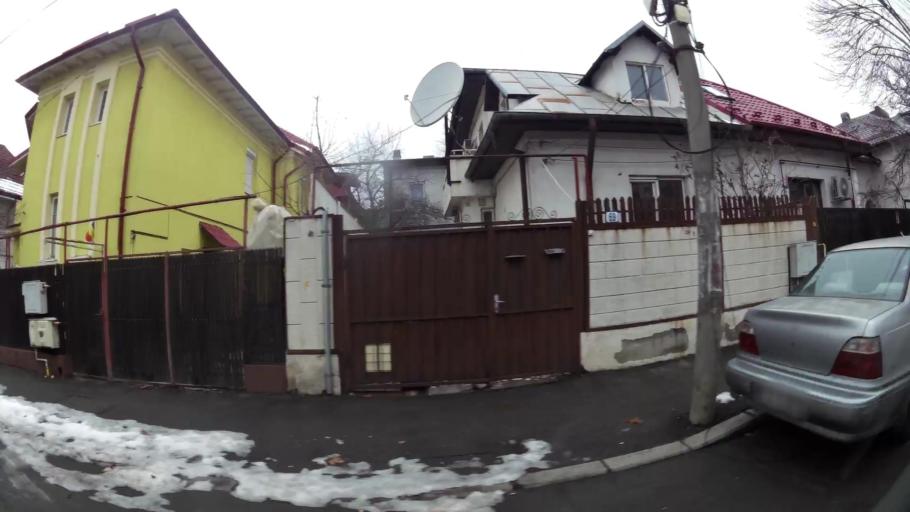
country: RO
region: Bucuresti
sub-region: Municipiul Bucuresti
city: Bucuresti
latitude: 44.4626
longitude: 26.0628
